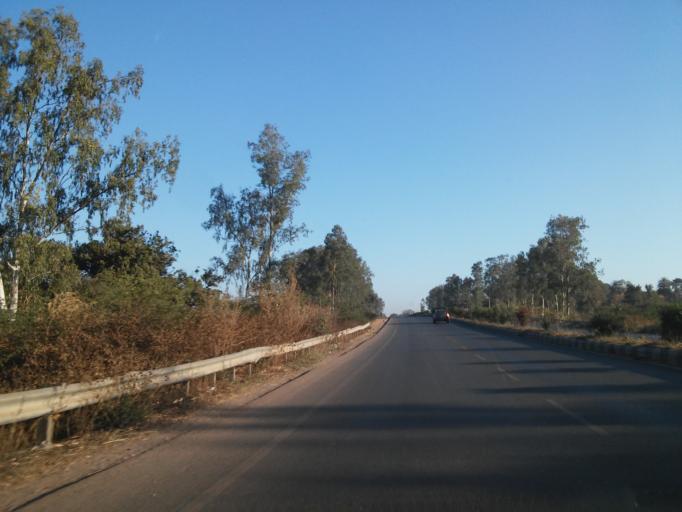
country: IN
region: Rajasthan
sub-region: Dungarpur
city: Dungarpur
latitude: 23.8415
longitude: 73.5240
